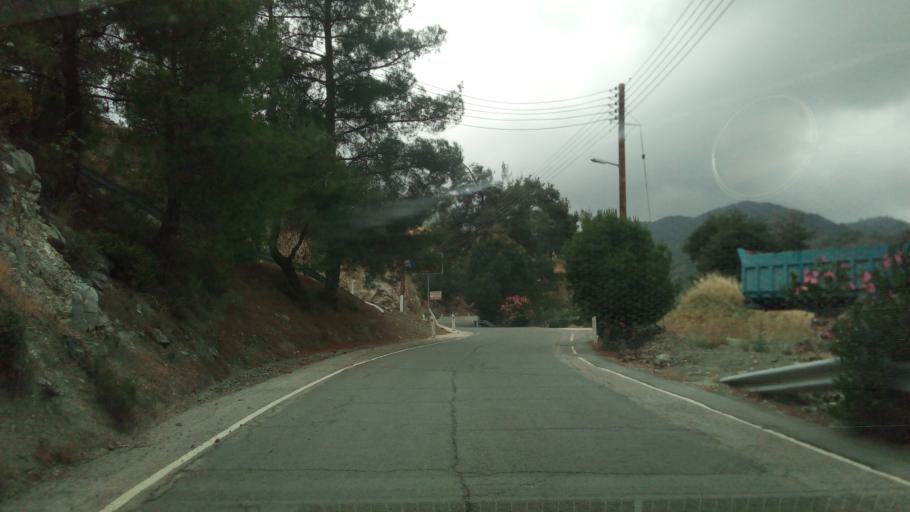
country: CY
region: Limassol
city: Pelendri
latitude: 34.8954
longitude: 33.0029
